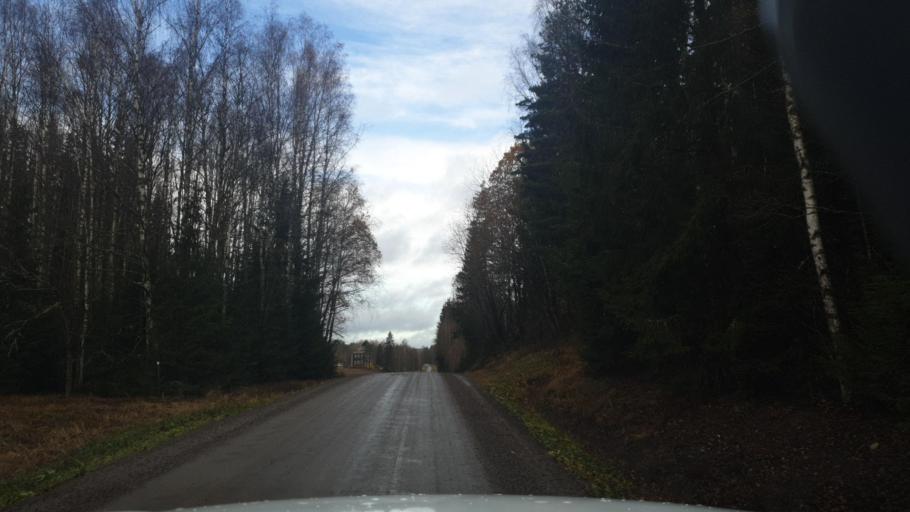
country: NO
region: Hedmark
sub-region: Eidskog
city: Skotterud
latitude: 59.8600
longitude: 11.9845
